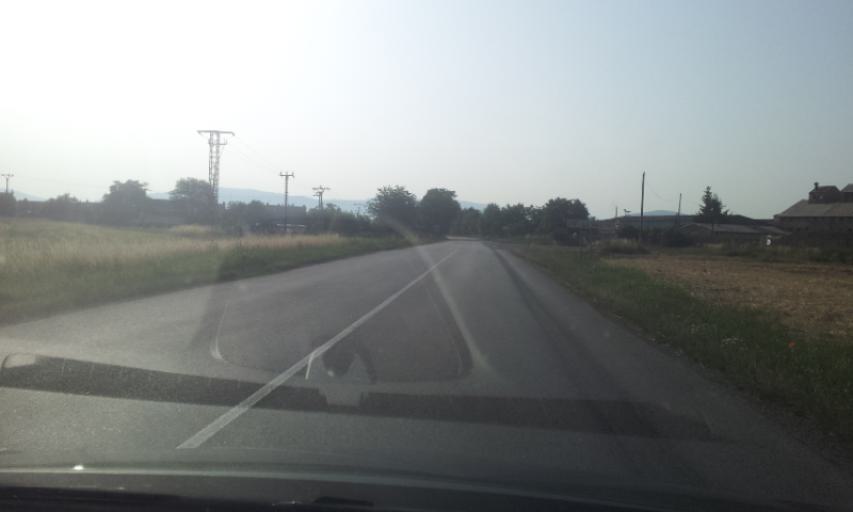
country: SK
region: Kosicky
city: Kosice
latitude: 48.6152
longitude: 21.2490
